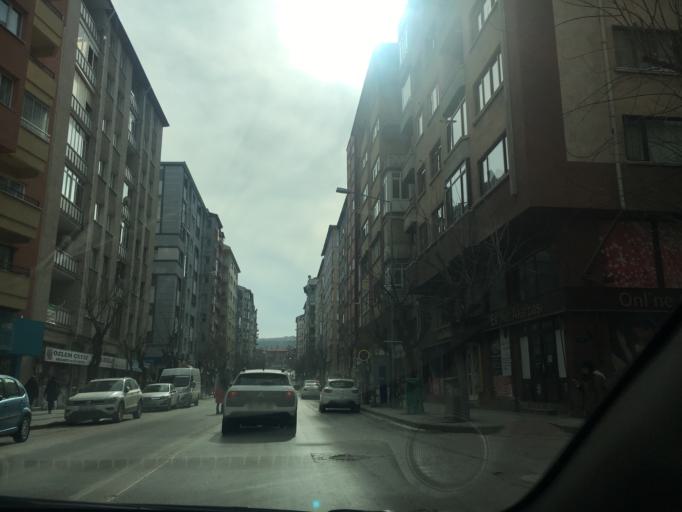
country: TR
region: Eskisehir
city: Eskisehir
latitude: 39.7677
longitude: 30.5187
